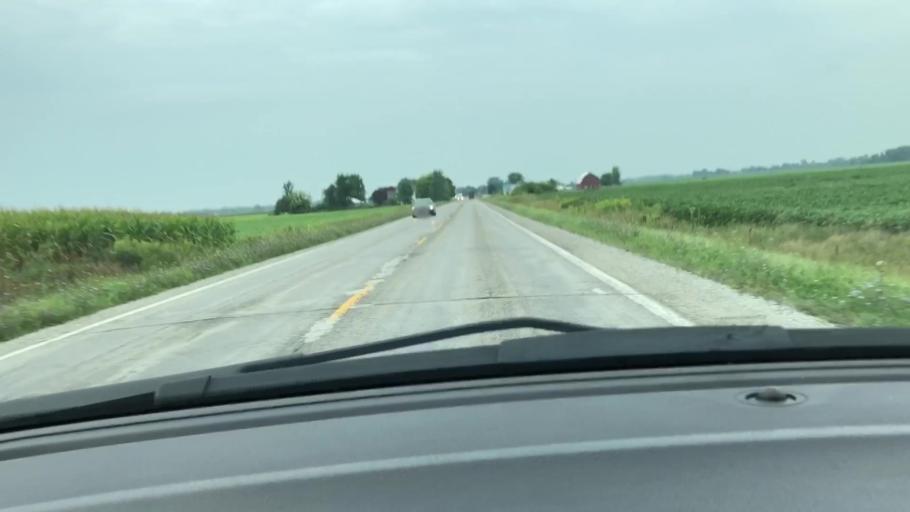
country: US
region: Michigan
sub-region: Bay County
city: Auburn
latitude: 43.5622
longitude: -84.0898
